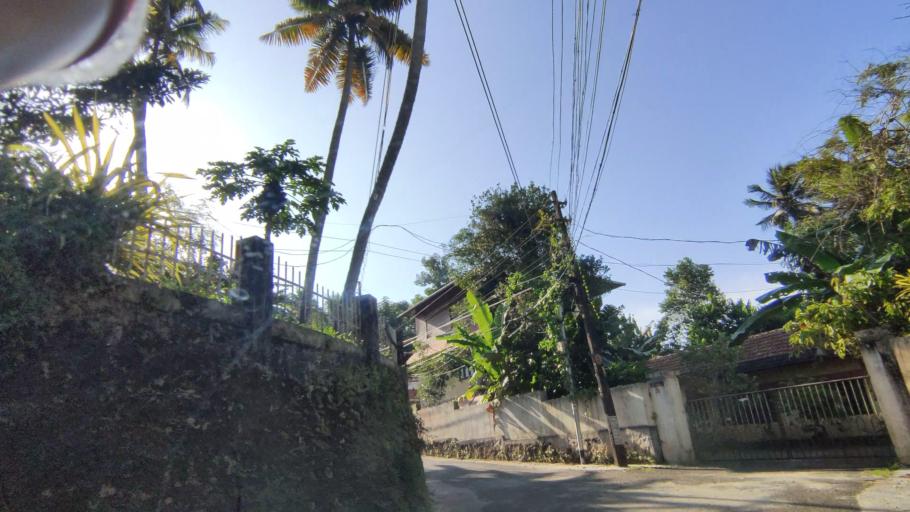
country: IN
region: Kerala
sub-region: Kottayam
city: Kottayam
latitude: 9.5928
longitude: 76.5114
